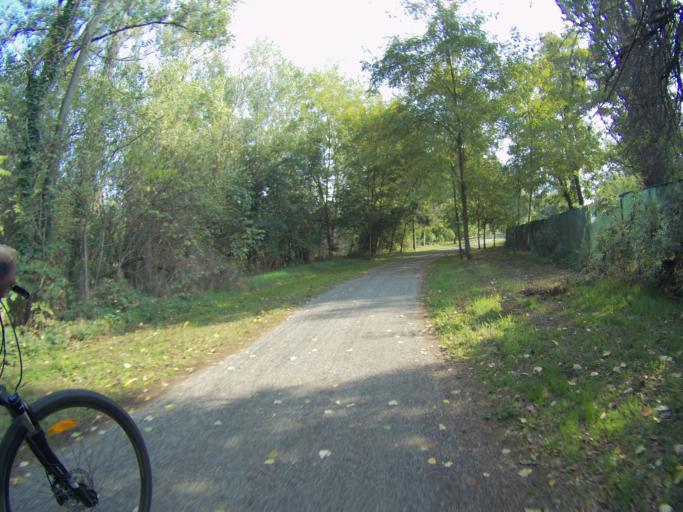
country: IT
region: Emilia-Romagna
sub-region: Provincia di Reggio Emilia
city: Albinea
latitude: 44.6653
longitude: 10.6015
